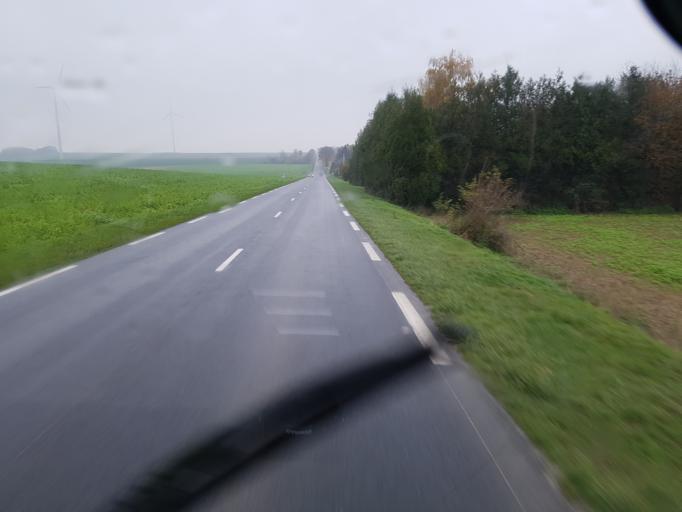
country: FR
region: Picardie
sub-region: Departement de l'Aisne
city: Saint-Quentin
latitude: 49.8914
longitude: 3.2649
